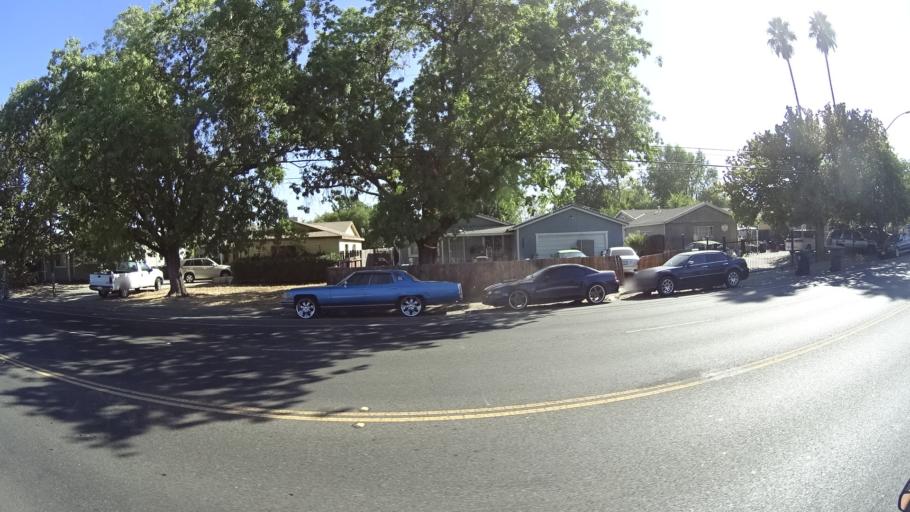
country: US
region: California
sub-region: Sacramento County
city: Parkway
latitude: 38.4884
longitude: -121.4804
